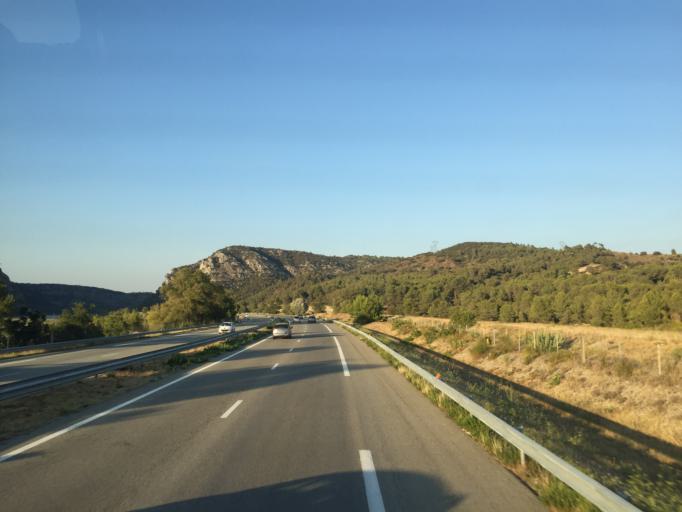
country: FR
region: Provence-Alpes-Cote d'Azur
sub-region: Departement des Bouches-du-Rhone
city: Jouques
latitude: 43.6715
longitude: 5.6451
